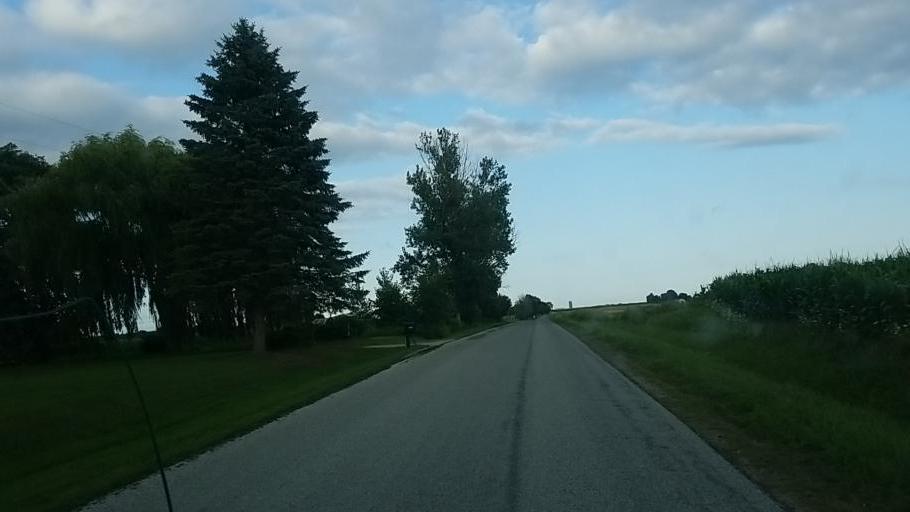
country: US
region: Michigan
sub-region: Montcalm County
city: Howard City
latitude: 43.3373
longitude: -85.3687
